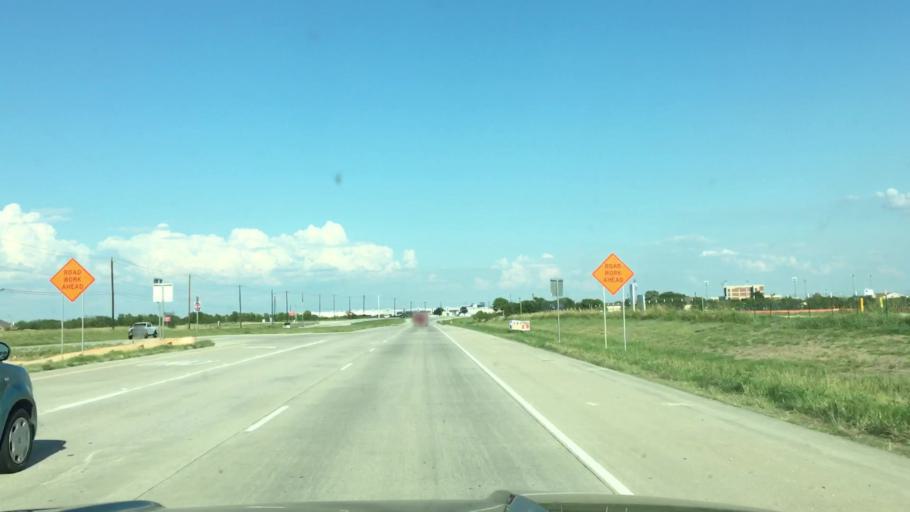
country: US
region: Texas
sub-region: Denton County
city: Justin
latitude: 33.0351
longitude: -97.3305
